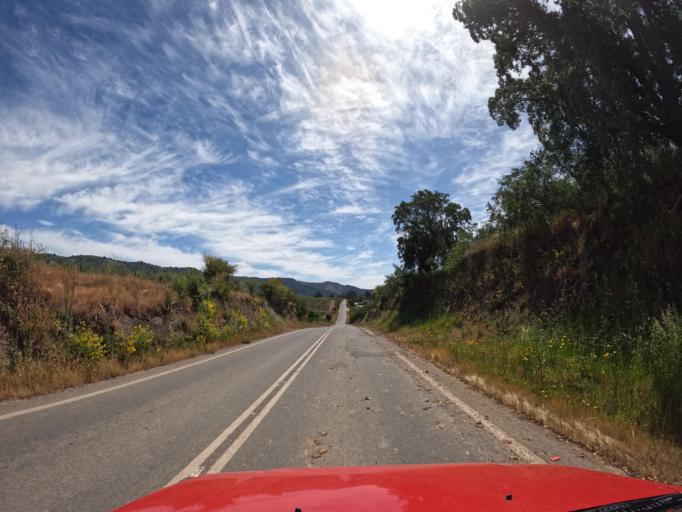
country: CL
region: Maule
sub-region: Provincia de Talca
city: Talca
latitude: -35.0150
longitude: -71.7767
